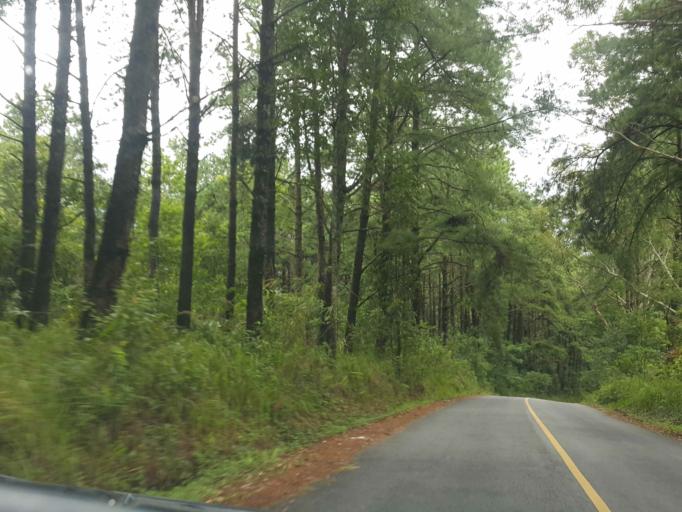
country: TH
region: Chiang Mai
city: Mae Chaem
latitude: 18.5177
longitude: 98.4793
